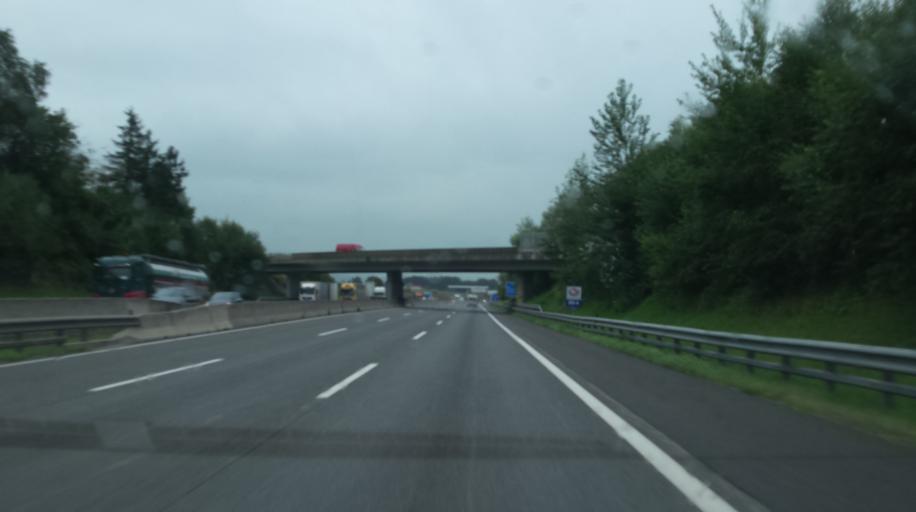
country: AT
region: Lower Austria
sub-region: Politischer Bezirk Amstetten
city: Amstetten
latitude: 48.1405
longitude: 14.8476
